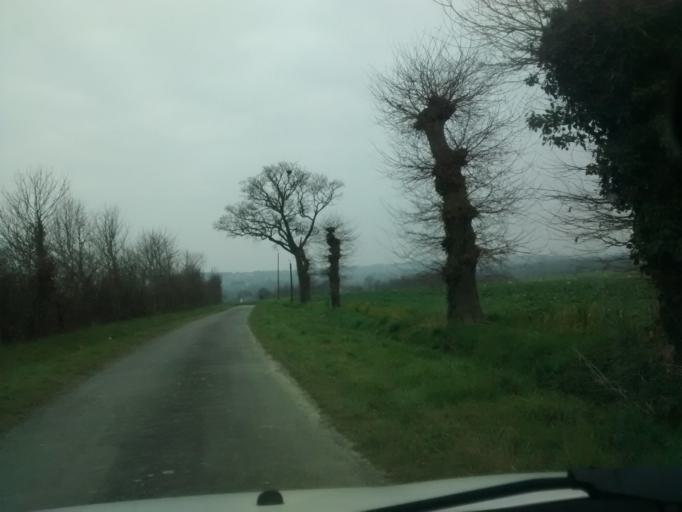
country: FR
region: Brittany
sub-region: Departement d'Ille-et-Vilaine
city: Bazouges-la-Perouse
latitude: 48.3946
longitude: -1.5923
